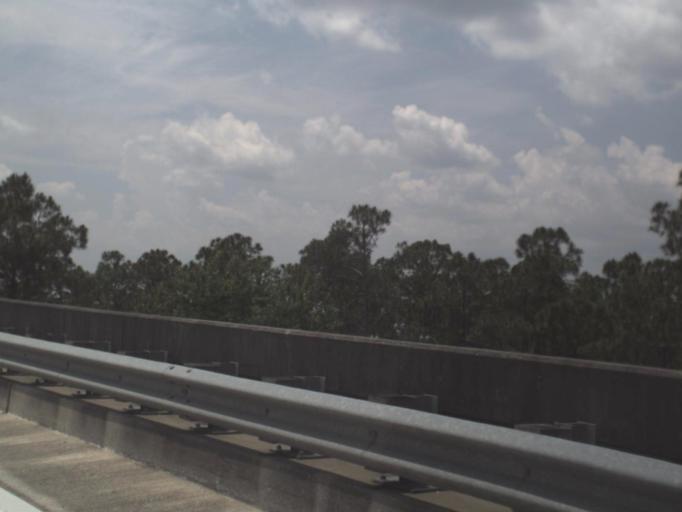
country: US
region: Florida
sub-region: Putnam County
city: Interlachen
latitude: 29.5361
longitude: -81.7567
